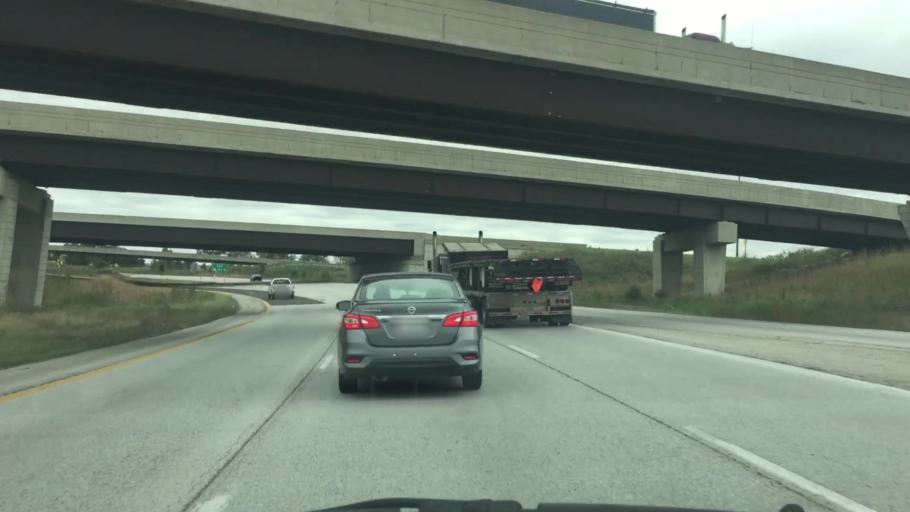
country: US
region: Iowa
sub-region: Polk County
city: Saylorville
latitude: 41.6508
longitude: -93.5776
